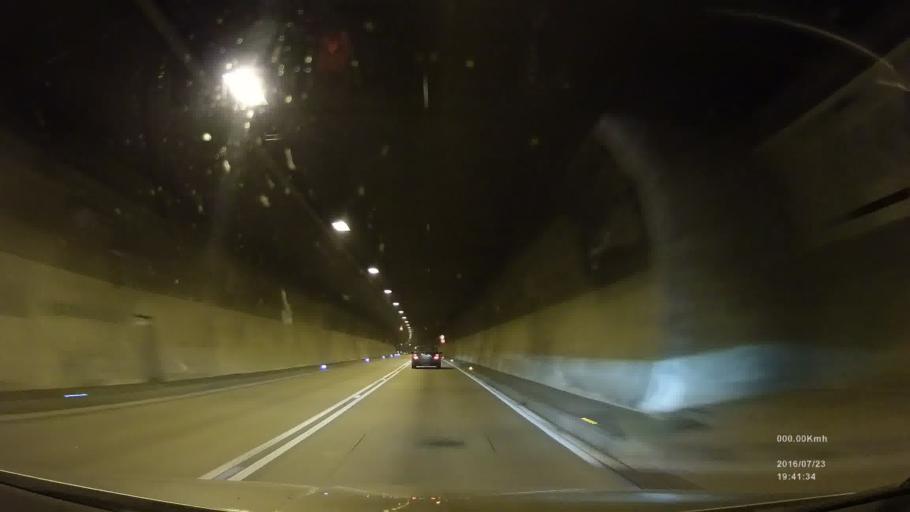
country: SK
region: Kosicky
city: Krompachy
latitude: 48.9982
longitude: 20.8980
